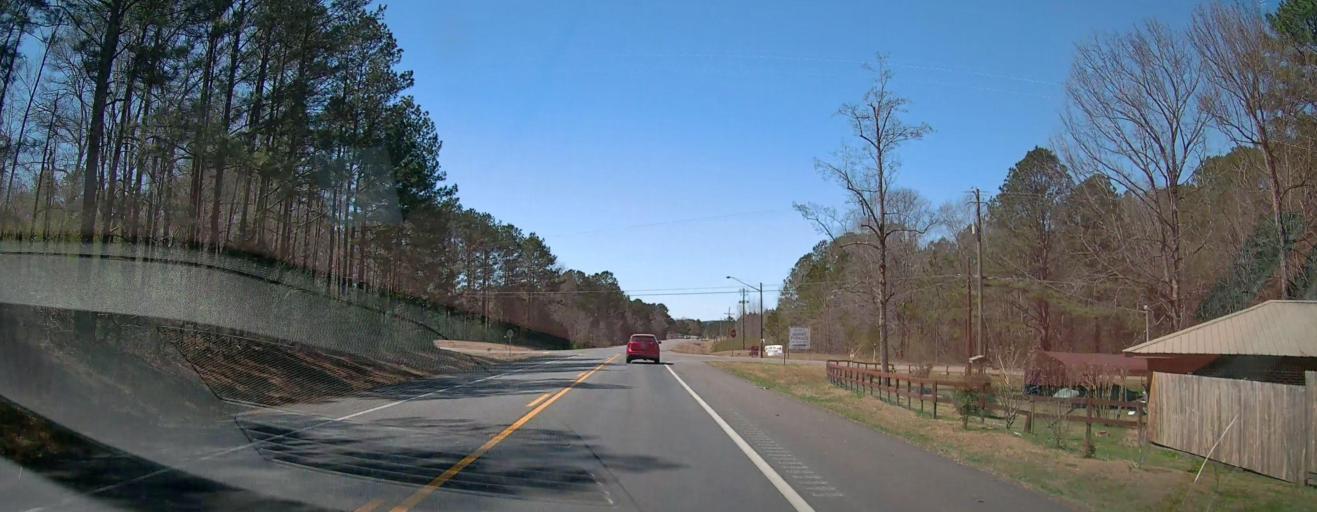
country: US
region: Alabama
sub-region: Calhoun County
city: Ohatchee
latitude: 33.7834
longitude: -86.0284
